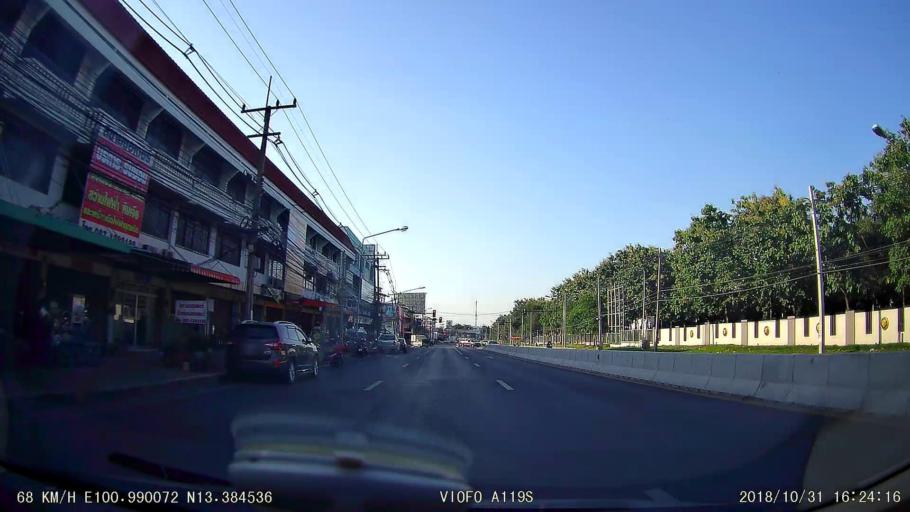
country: TH
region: Chon Buri
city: Chon Buri
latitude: 13.3848
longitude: 100.9899
